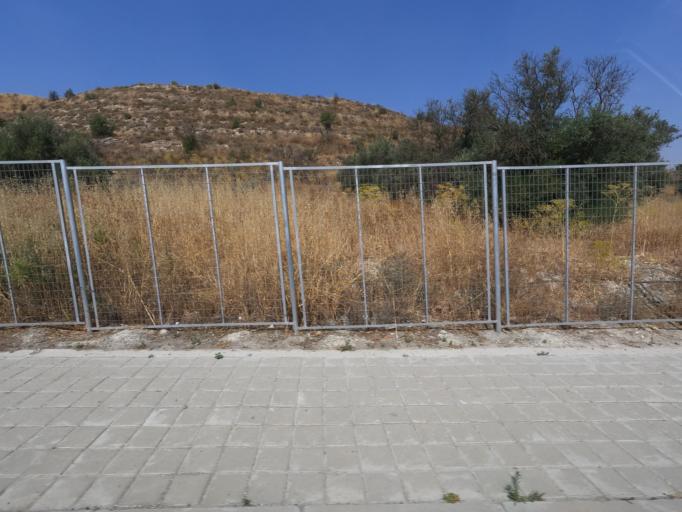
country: CY
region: Lefkosia
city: Dali
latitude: 35.0155
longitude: 33.4253
